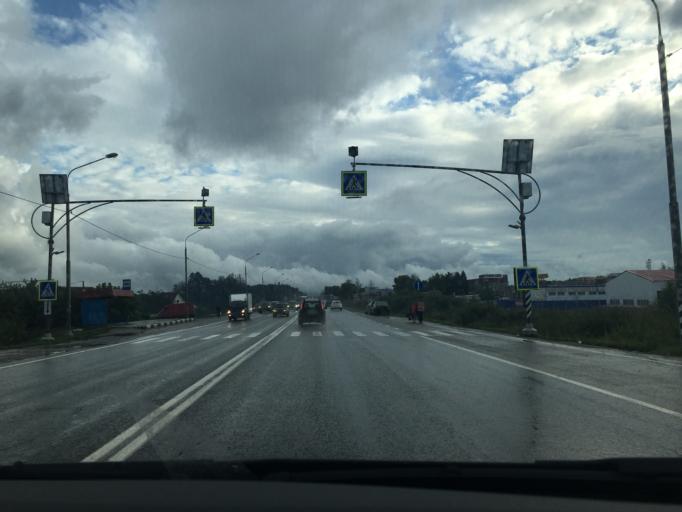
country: RU
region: Kaluga
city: Belousovo
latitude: 55.1161
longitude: 36.6463
